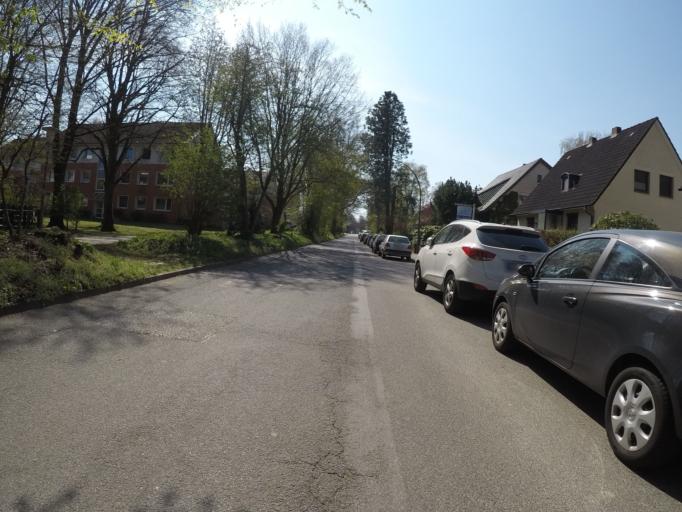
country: DE
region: Schleswig-Holstein
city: Halstenbek
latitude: 53.5842
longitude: 9.8173
